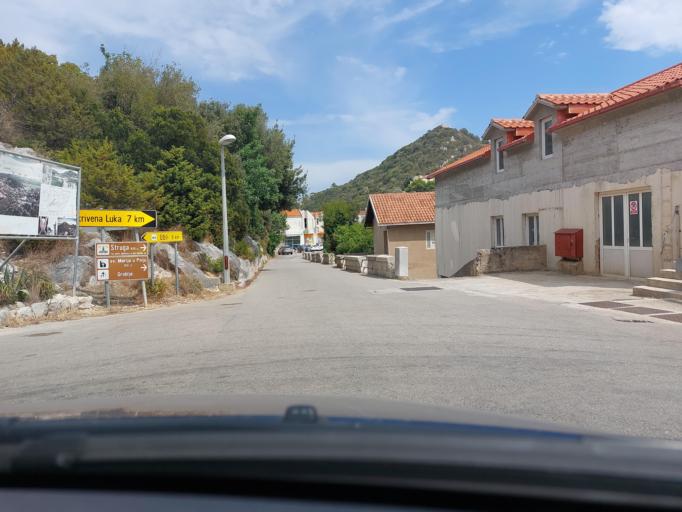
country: HR
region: Dubrovacko-Neretvanska
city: Smokvica
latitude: 42.7689
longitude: 16.8941
